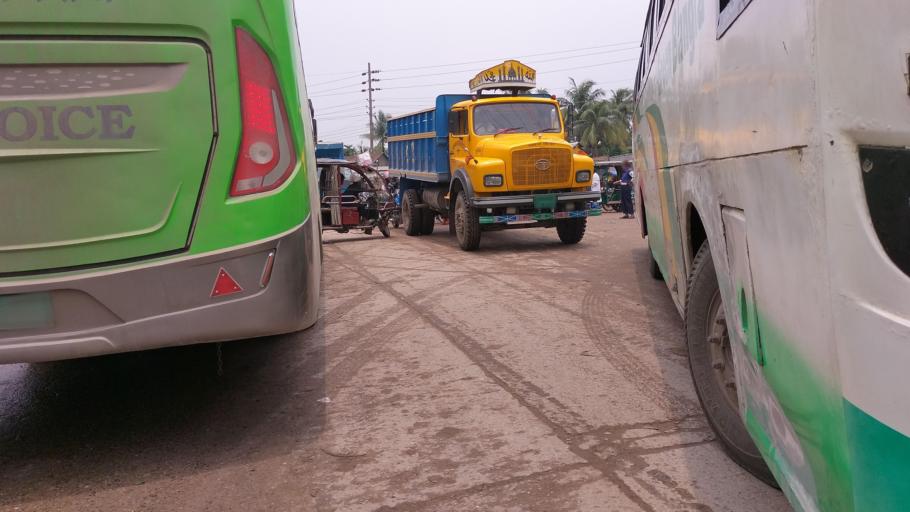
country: BD
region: Dhaka
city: Mymensingh
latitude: 24.7626
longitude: 90.4505
